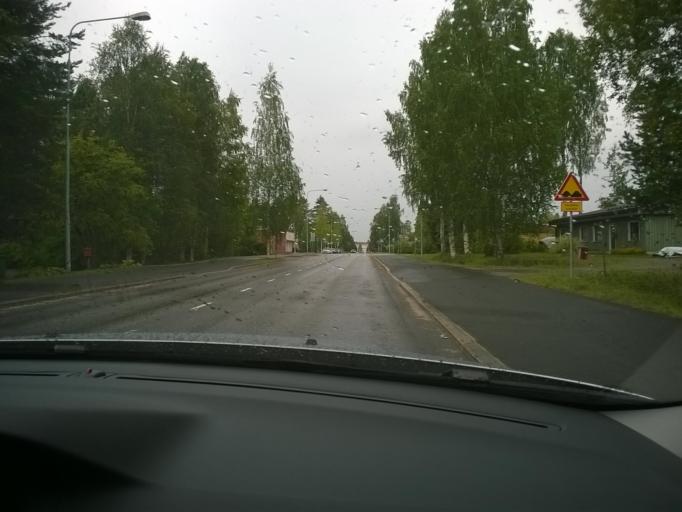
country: FI
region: Kainuu
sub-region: Kehys-Kainuu
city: Kuhmo
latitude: 64.1243
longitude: 29.5319
